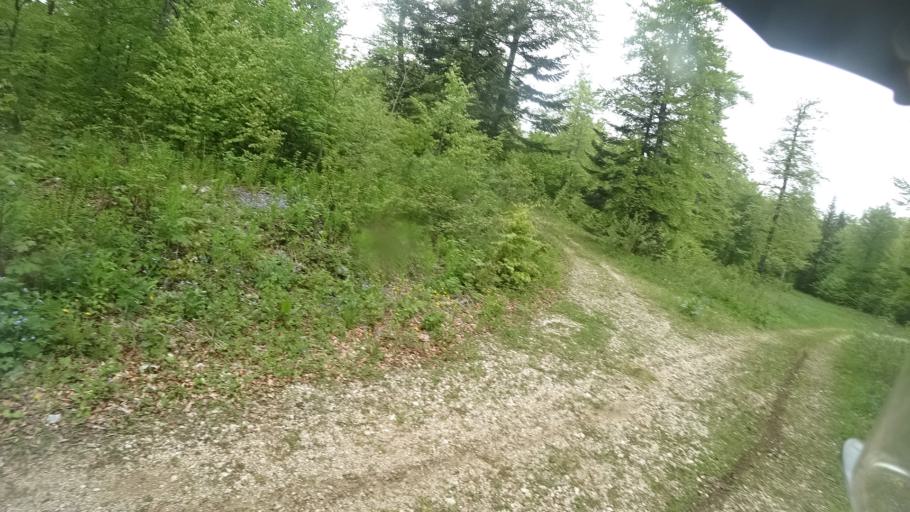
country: BA
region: Federation of Bosnia and Herzegovina
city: Orasac
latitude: 44.5654
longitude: 15.8836
